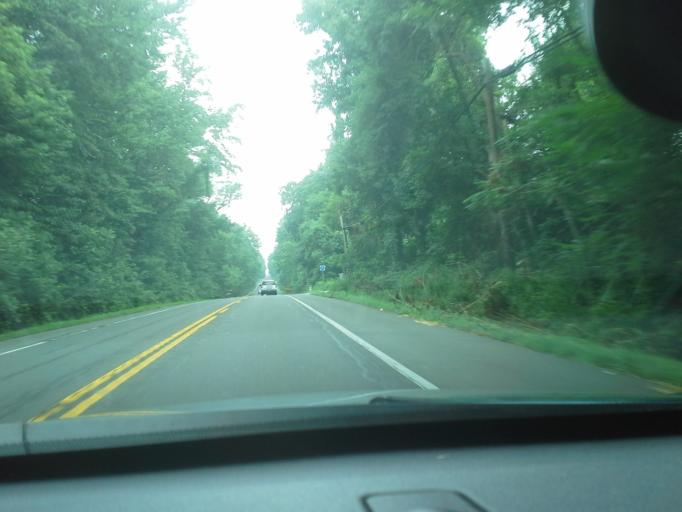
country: US
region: Maryland
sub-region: Calvert County
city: Owings
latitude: 38.7370
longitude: -76.6252
